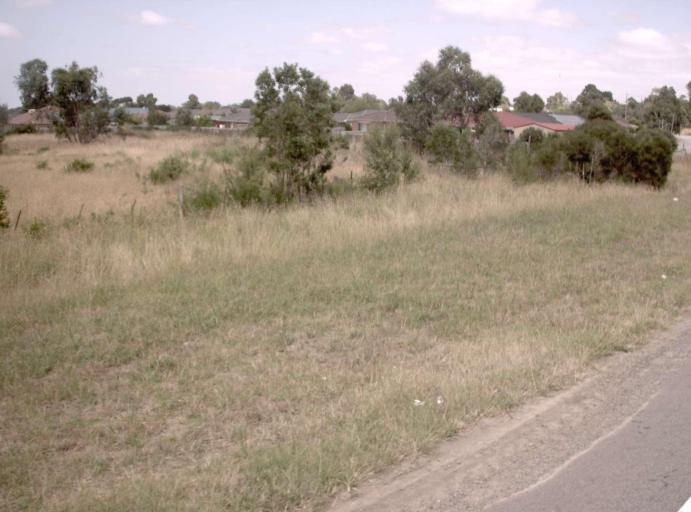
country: AU
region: Victoria
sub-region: Cardinia
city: Pakenham Upper
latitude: -38.0662
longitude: 145.5018
